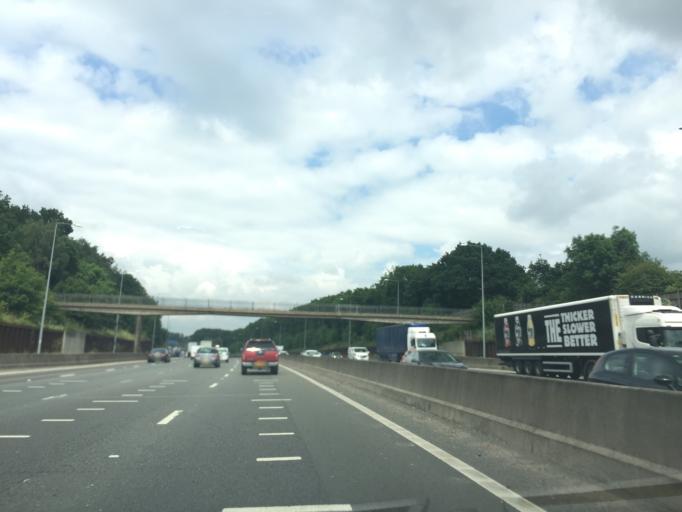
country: GB
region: England
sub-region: Hertfordshire
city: Chorleywood
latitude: 51.6442
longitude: -0.5013
